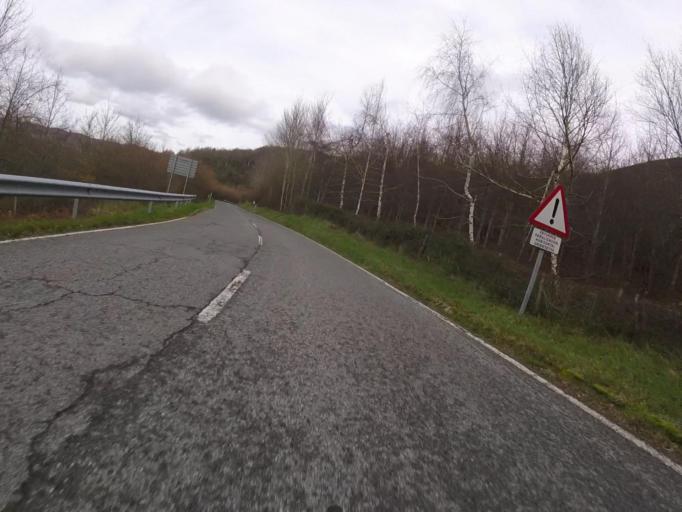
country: ES
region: Navarre
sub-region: Provincia de Navarra
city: Olazagutia
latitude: 42.8709
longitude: -2.1843
